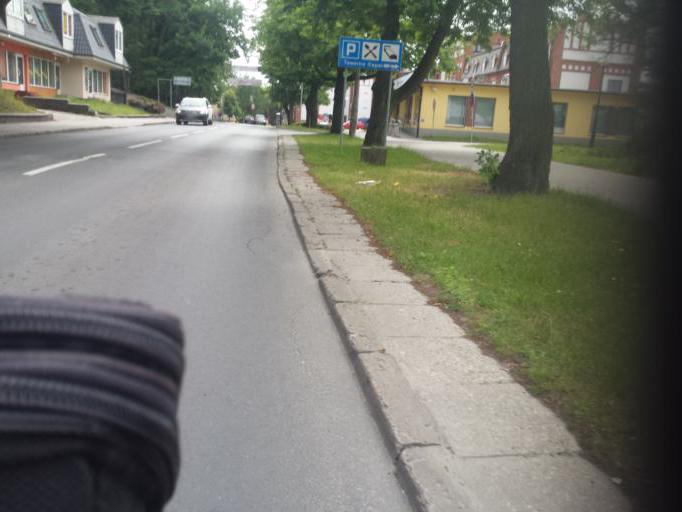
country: PL
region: Warmian-Masurian Voivodeship
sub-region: Powiat ilawski
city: Ilawa
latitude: 53.5942
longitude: 19.5653
